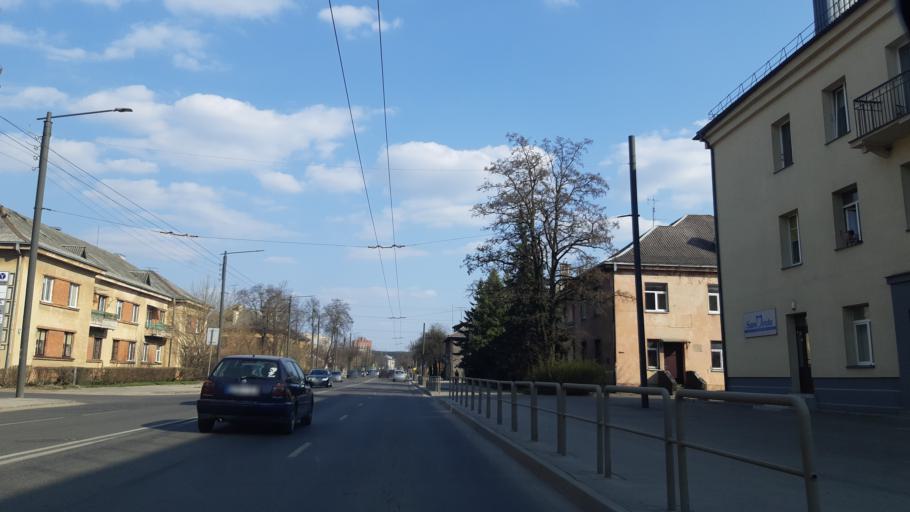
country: LT
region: Kauno apskritis
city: Dainava (Kaunas)
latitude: 54.8943
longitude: 23.9896
